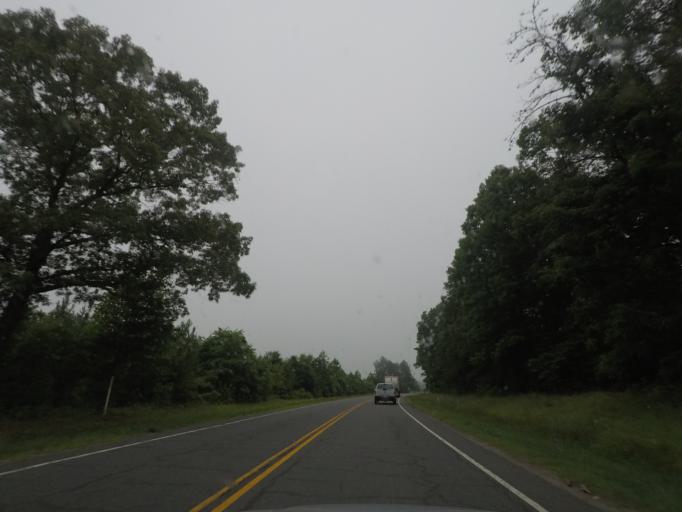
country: US
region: Virginia
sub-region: Buckingham County
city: Buckingham
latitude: 37.5091
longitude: -78.4880
